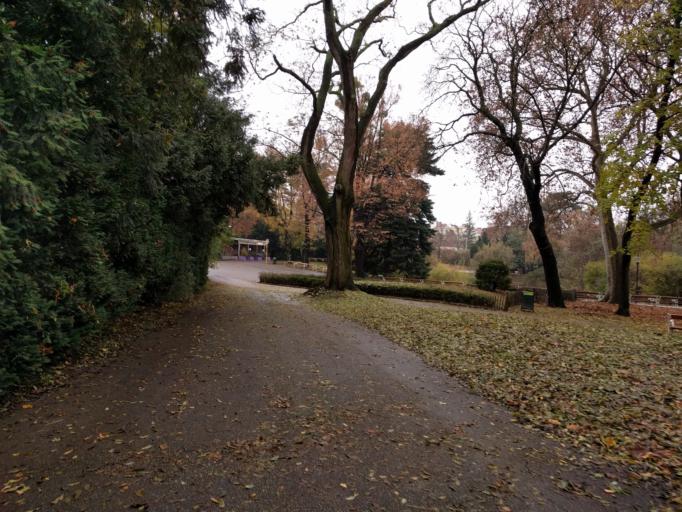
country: AT
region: Vienna
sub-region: Wien Stadt
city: Vienna
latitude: 48.2352
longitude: 16.3316
